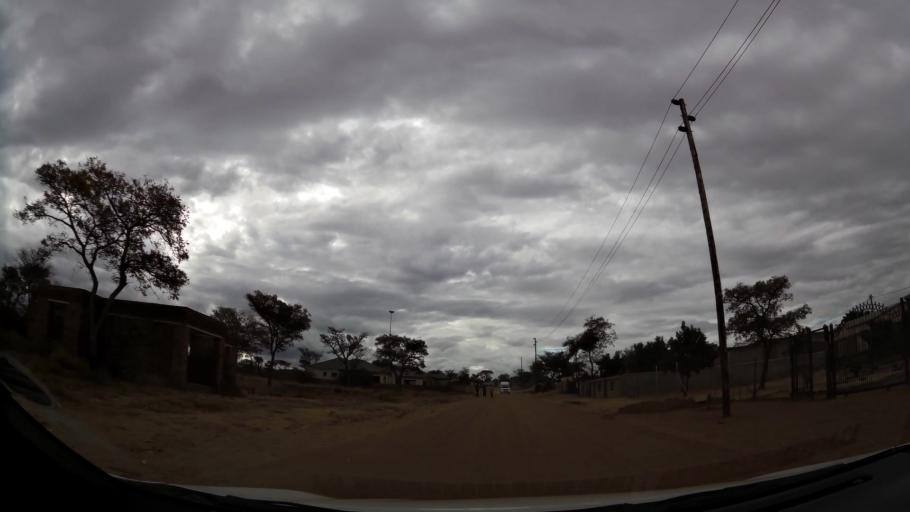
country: ZA
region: Limpopo
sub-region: Waterberg District Municipality
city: Modimolle
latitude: -24.6967
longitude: 28.4246
